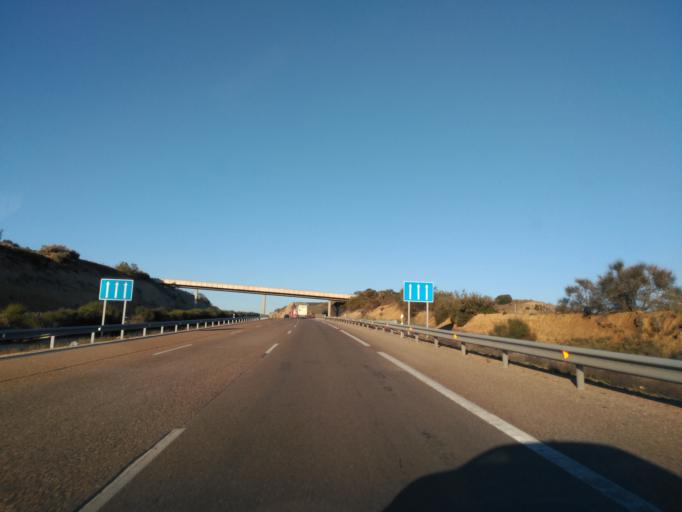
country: ES
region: Castille and Leon
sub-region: Provincia de Zamora
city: Castrillo de la Guarena
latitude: 41.2368
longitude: -5.3052
